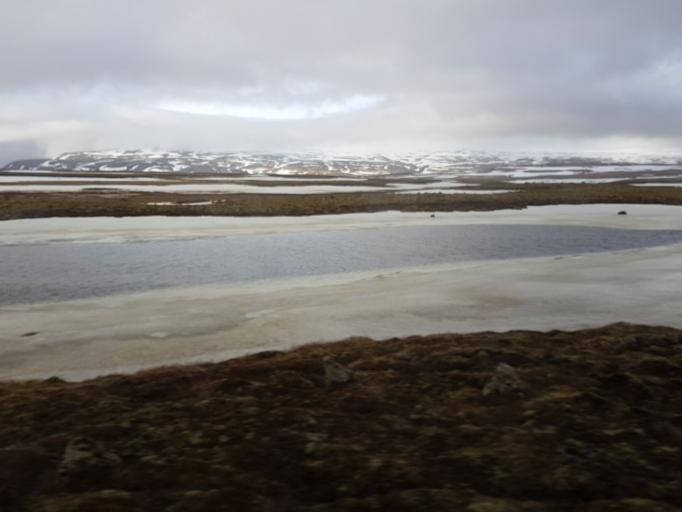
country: IS
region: South
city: Hveragerdi
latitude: 64.2096
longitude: -21.3072
